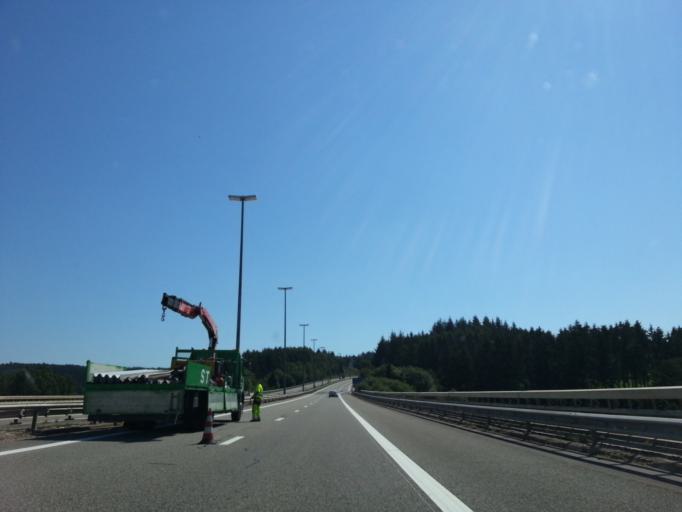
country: BE
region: Wallonia
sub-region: Province de Liege
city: Saint-Vith
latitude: 50.2613
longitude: 6.1502
